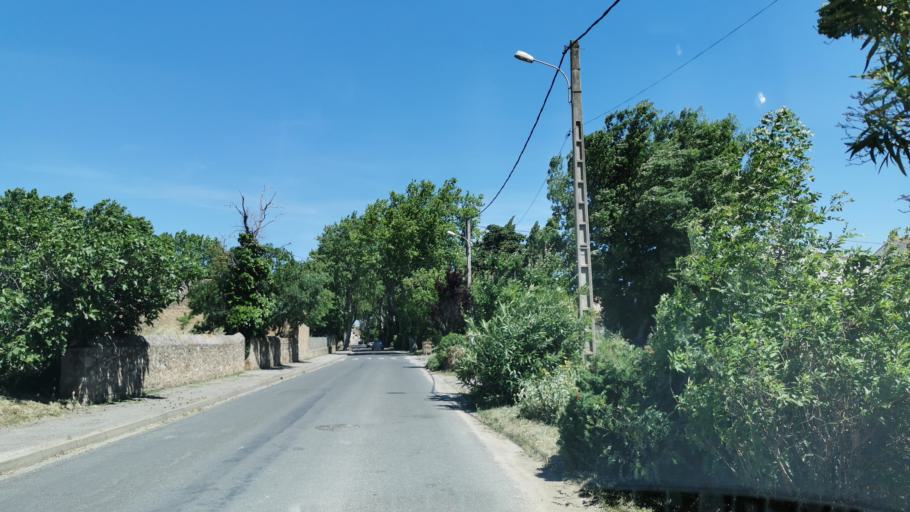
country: FR
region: Languedoc-Roussillon
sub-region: Departement de l'Aude
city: Canet
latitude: 43.2239
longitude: 2.8466
